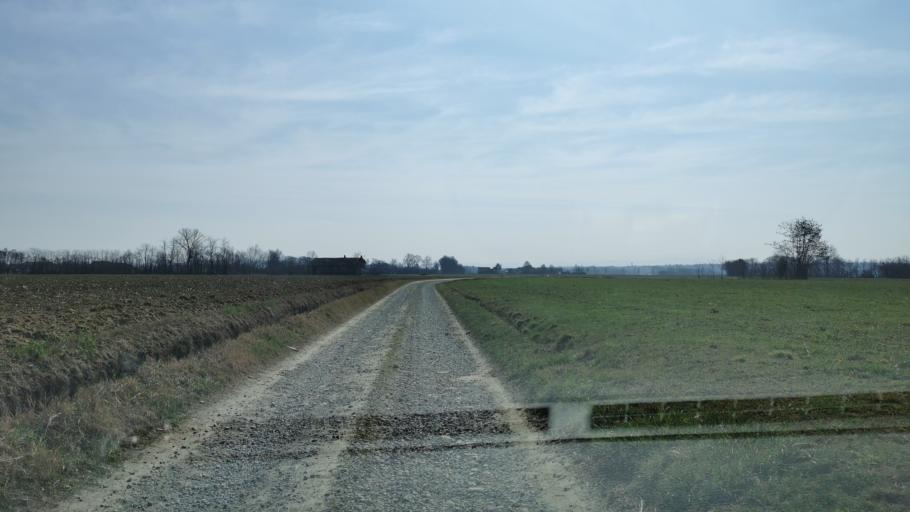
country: IT
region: Piedmont
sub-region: Provincia di Torino
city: Rivarossa
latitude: 45.2819
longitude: 7.7173
